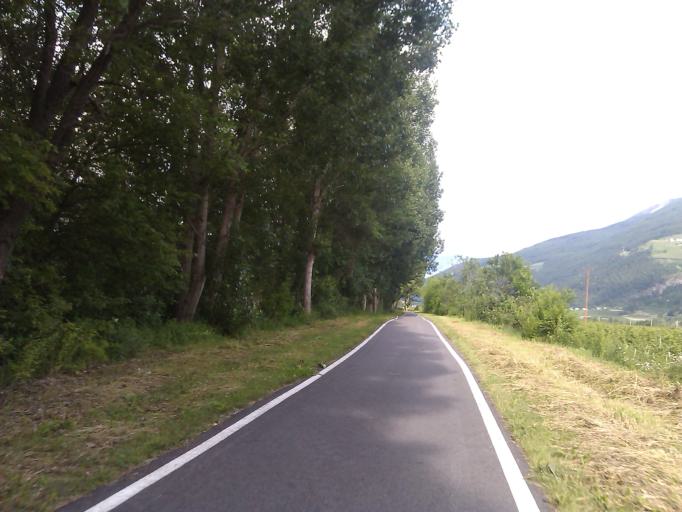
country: IT
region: Trentino-Alto Adige
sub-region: Bolzano
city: Lasa
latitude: 46.6196
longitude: 10.6705
